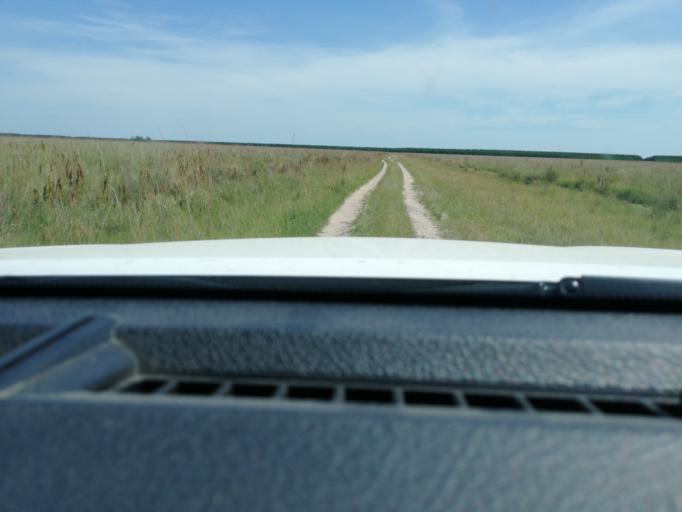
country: AR
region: Corrientes
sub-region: Departamento de San Miguel
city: San Miguel
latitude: -28.0521
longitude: -57.4554
